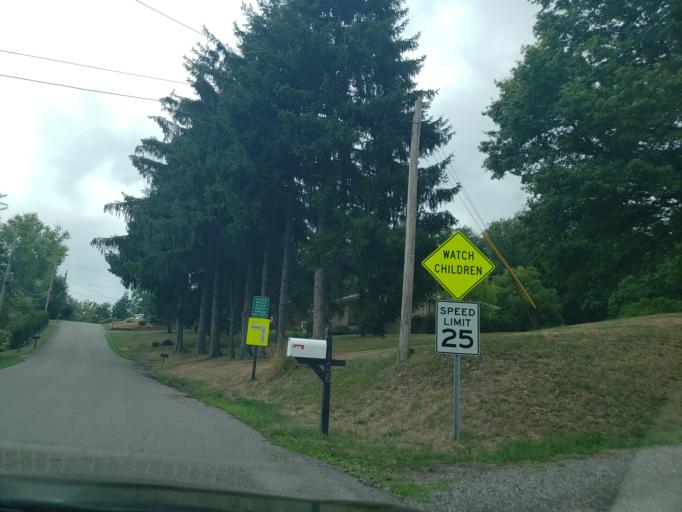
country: US
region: Pennsylvania
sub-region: Allegheny County
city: Coraopolis
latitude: 40.5404
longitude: -80.1553
